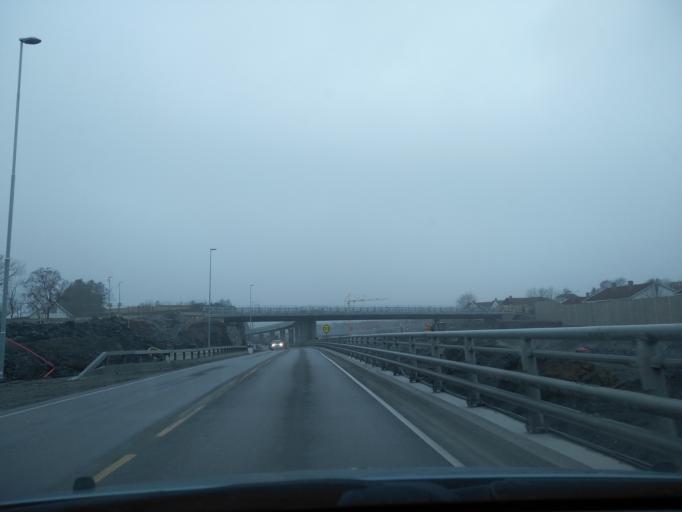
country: NO
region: Rogaland
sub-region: Stavanger
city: Stavanger
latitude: 58.9761
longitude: 5.6897
